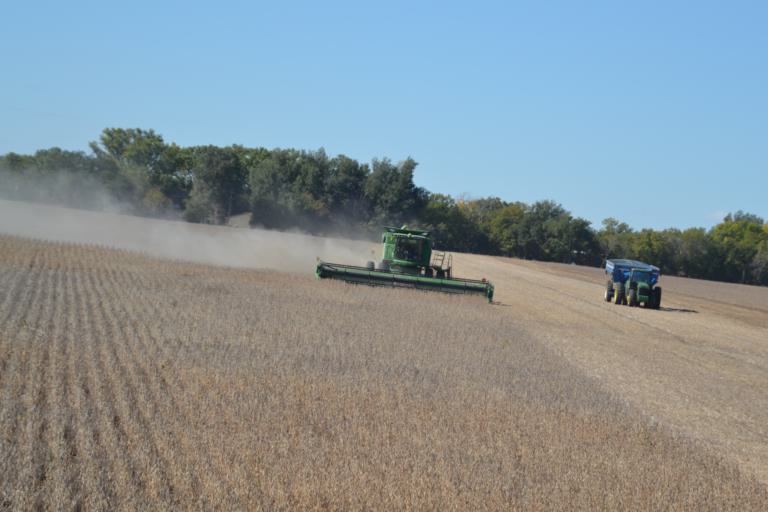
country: US
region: Kansas
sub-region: Barton County
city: Great Bend
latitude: 38.3602
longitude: -98.7034
